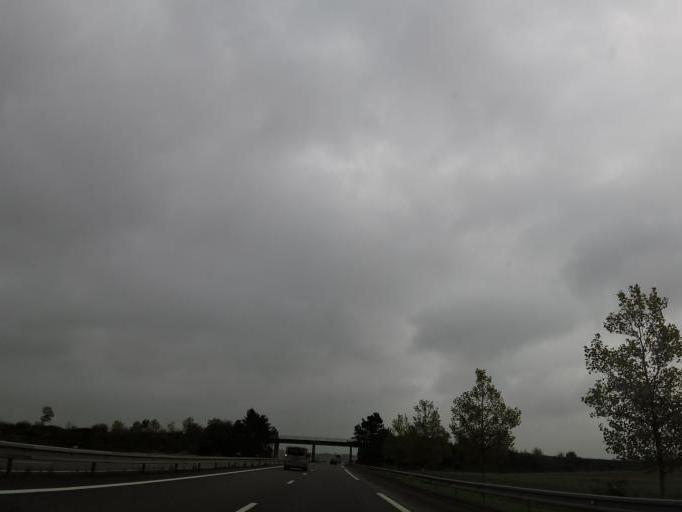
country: FR
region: Champagne-Ardenne
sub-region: Departement de la Marne
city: Saint-Memmie
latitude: 49.0346
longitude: 4.3835
